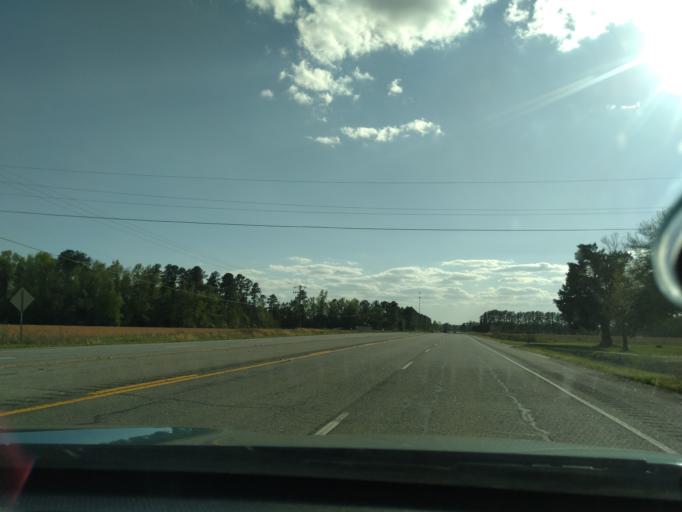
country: US
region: South Carolina
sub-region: Williamsburg County
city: Kingstree
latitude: 33.6478
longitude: -79.8889
